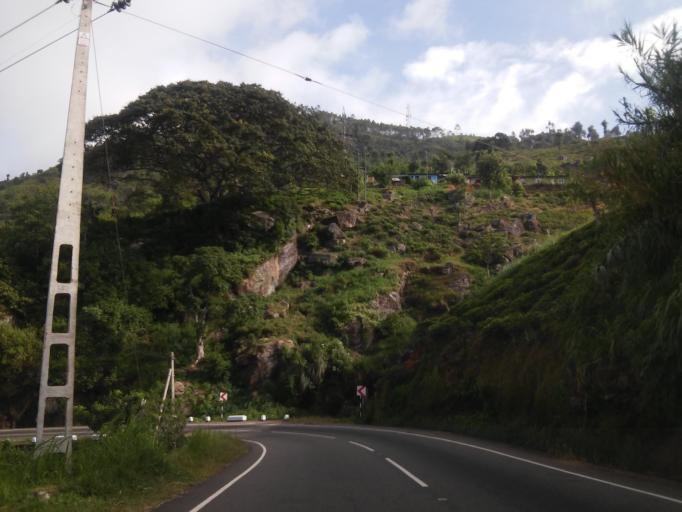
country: LK
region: Uva
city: Haputale
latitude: 6.7593
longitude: 80.9427
